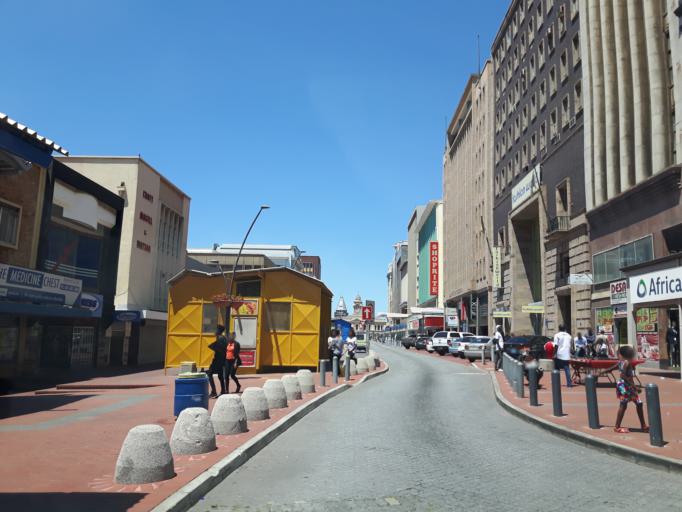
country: ZA
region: Eastern Cape
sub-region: Nelson Mandela Bay Metropolitan Municipality
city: Port Elizabeth
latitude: -33.9598
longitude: 25.6213
